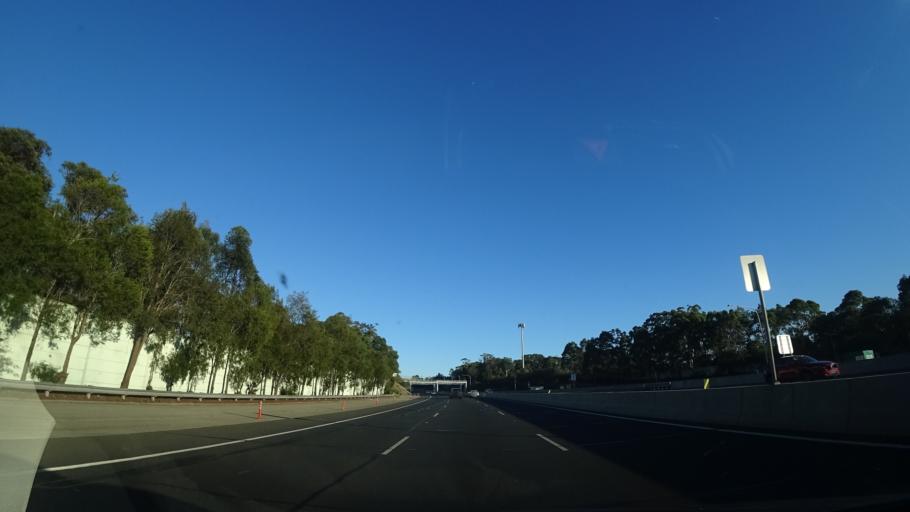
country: AU
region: New South Wales
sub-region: Ryde
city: Macquarie Park
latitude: -33.7689
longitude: 151.1156
